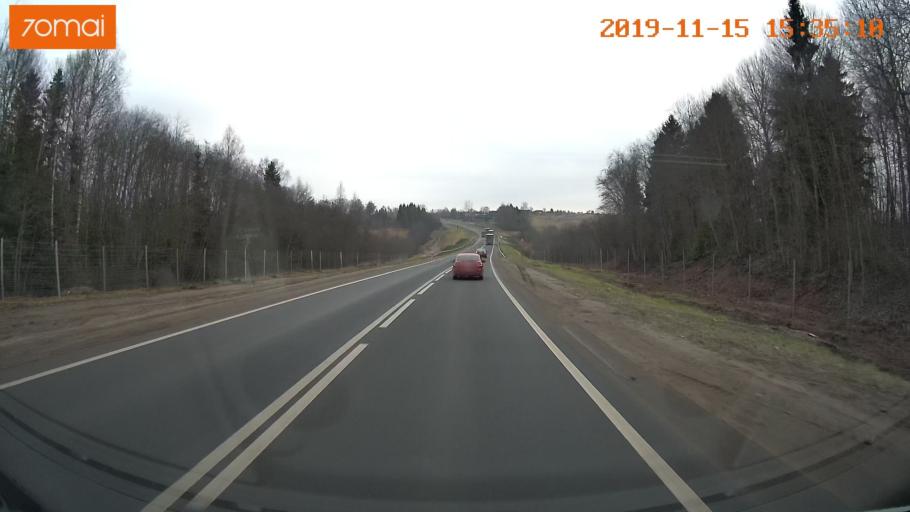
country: RU
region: Jaroslavl
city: Danilov
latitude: 58.0619
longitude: 40.0881
